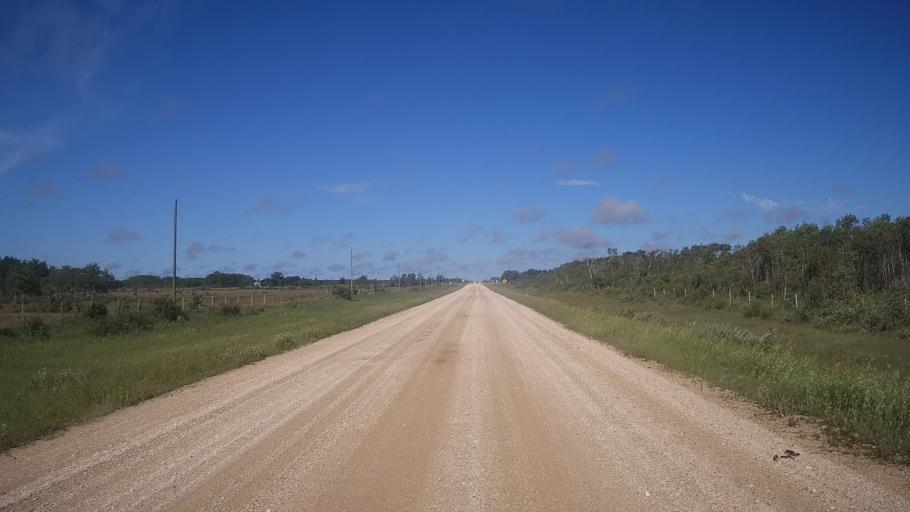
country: CA
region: Manitoba
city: Stonewall
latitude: 50.2411
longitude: -97.7277
